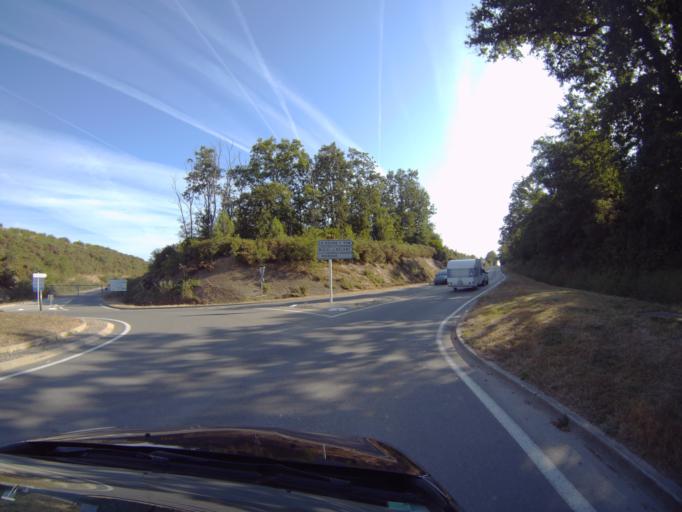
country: FR
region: Pays de la Loire
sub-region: Departement de la Vendee
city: Saint-Hilaire-de-Talmont
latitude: 46.4744
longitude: -1.6044
